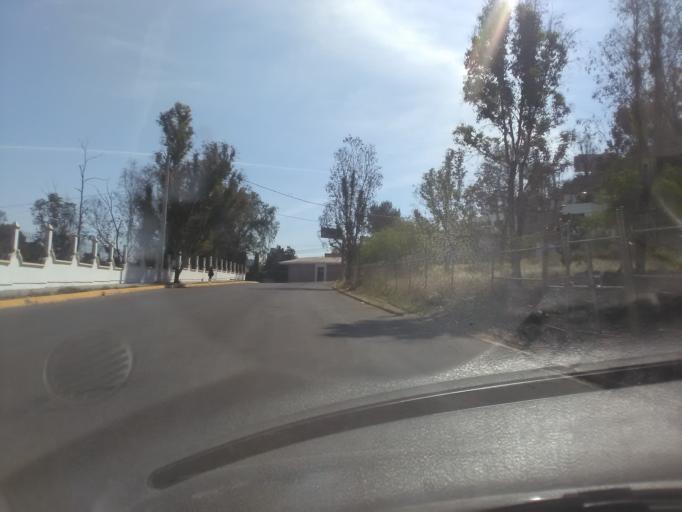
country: MX
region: Durango
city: Victoria de Durango
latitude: 24.0238
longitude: -104.6842
